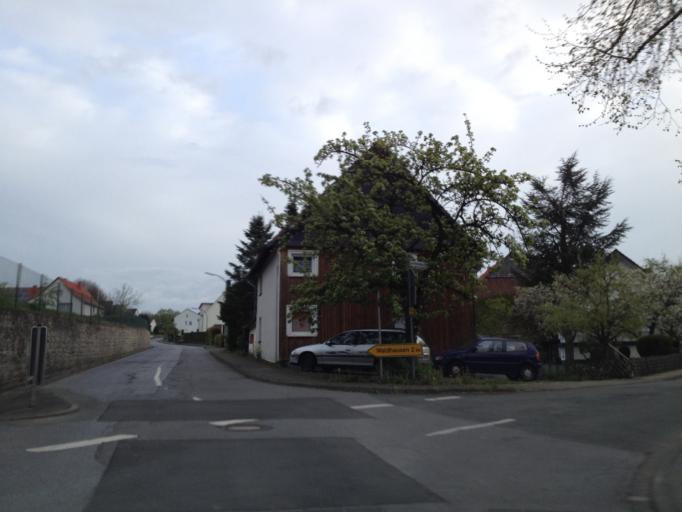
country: DE
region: North Rhine-Westphalia
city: Warstein
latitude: 51.4919
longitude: 8.2867
